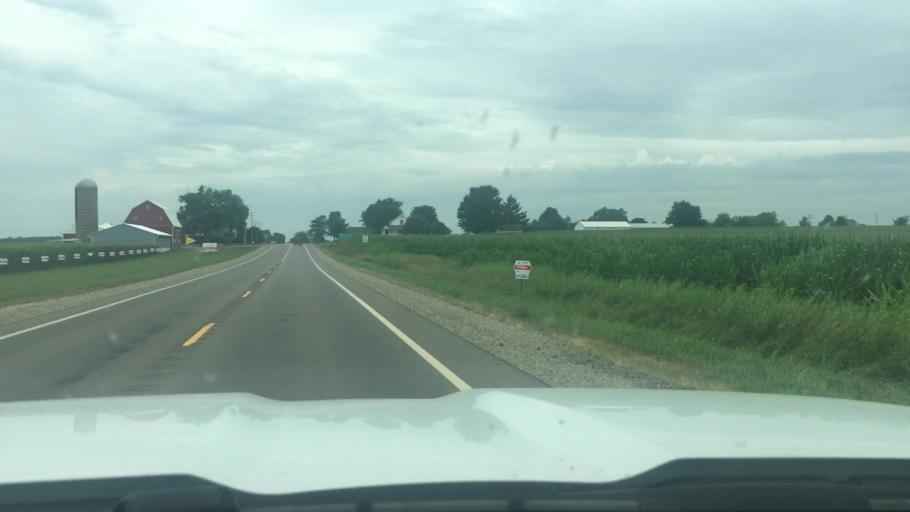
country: US
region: Michigan
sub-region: Clinton County
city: Fowler
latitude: 43.0017
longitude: -84.6758
